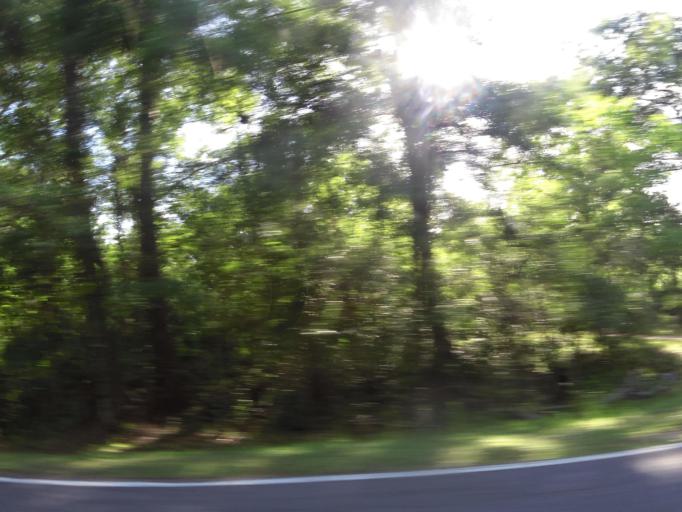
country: US
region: Florida
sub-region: Nassau County
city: Nassau Village-Ratliff
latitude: 30.4686
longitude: -81.7844
